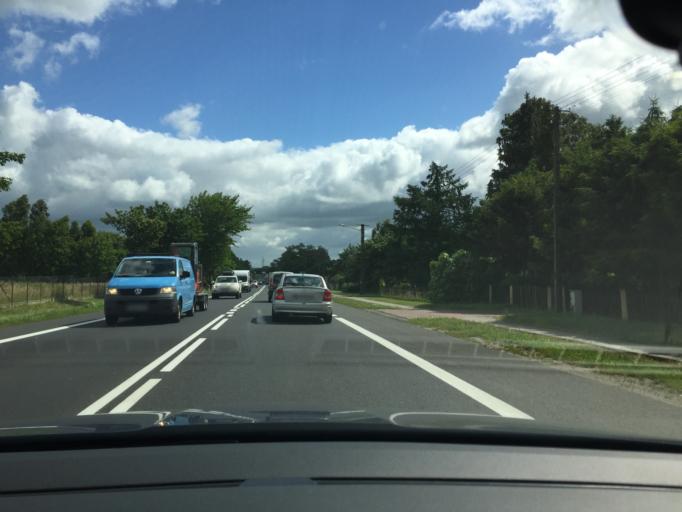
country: PL
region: West Pomeranian Voivodeship
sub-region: Powiat slawienski
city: Slawno
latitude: 54.3448
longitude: 16.6535
